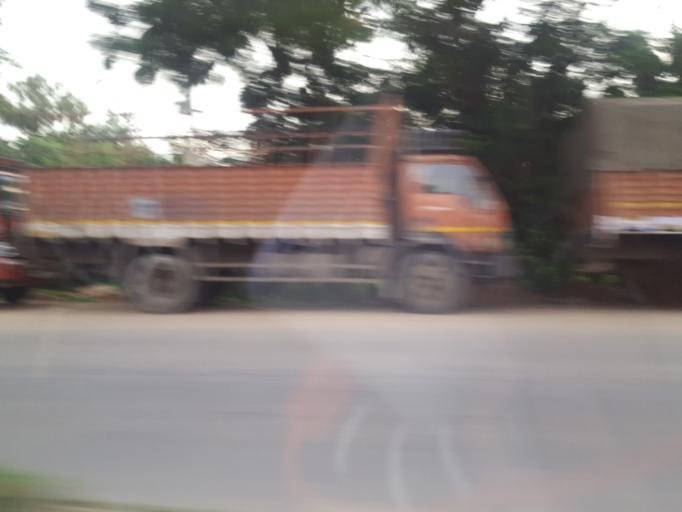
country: IN
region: Telangana
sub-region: Medak
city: Serilingampalle
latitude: 17.5167
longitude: 78.3573
